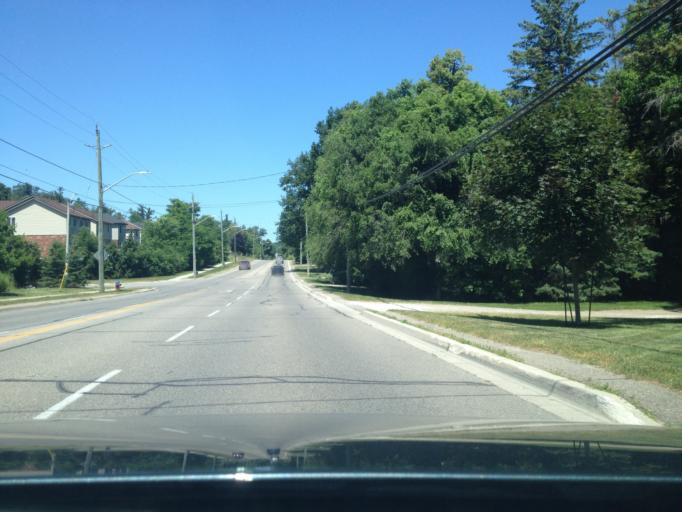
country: CA
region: Ontario
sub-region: Halton
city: Milton
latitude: 43.6609
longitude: -79.9177
